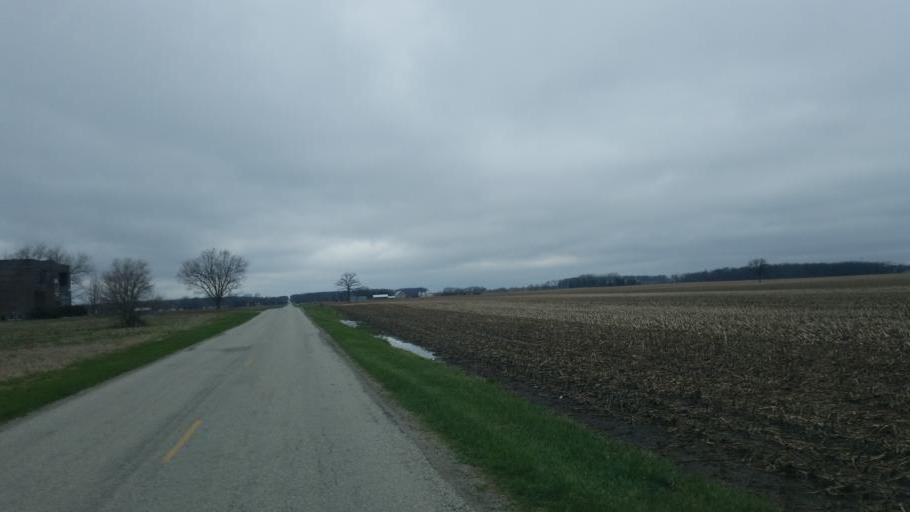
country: US
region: Ohio
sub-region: Marion County
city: Marion
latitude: 40.6737
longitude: -83.1280
